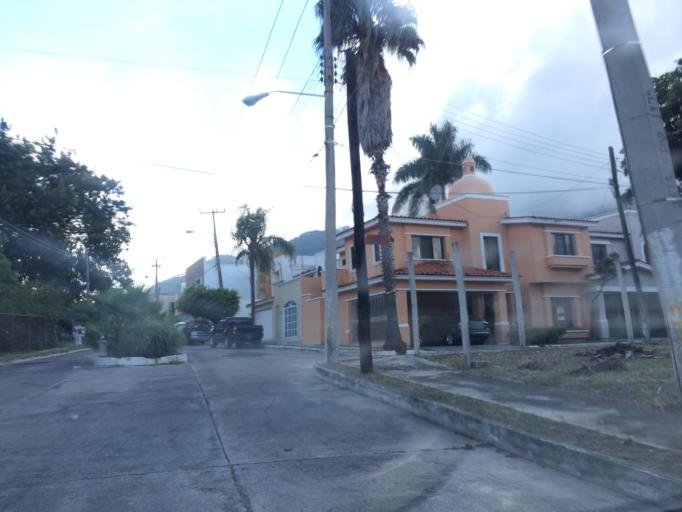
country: MX
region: Nayarit
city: Tepic
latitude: 21.5041
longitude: -104.9053
